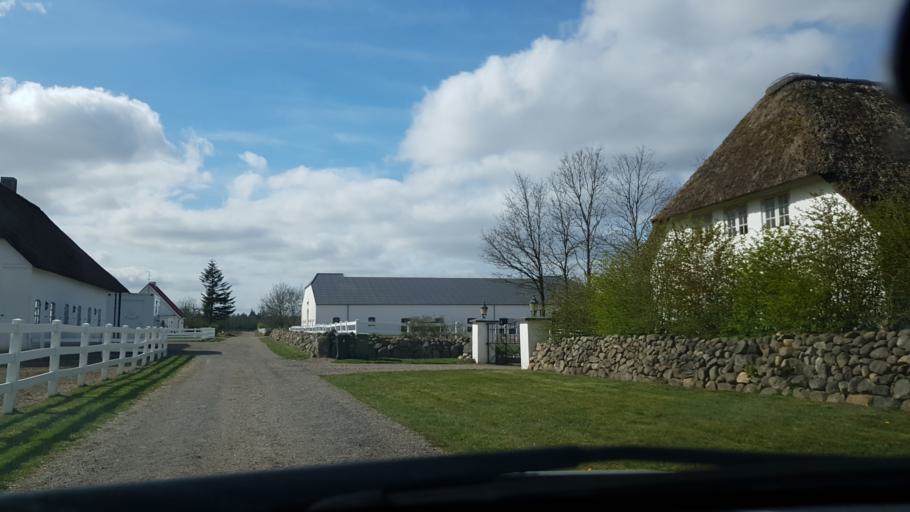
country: DK
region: South Denmark
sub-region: Haderslev Kommune
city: Gram
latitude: 55.2986
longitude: 8.9841
